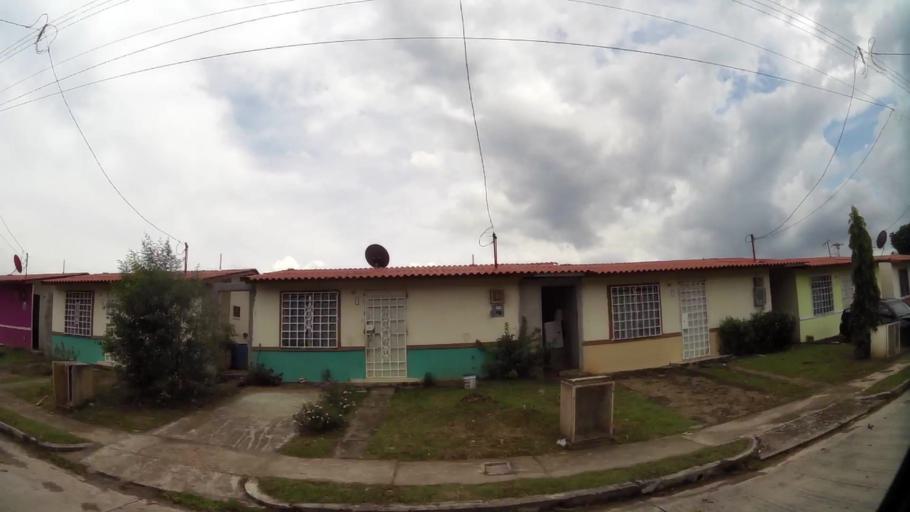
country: PA
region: Panama
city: Cabra Numero Uno
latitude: 9.1165
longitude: -79.3250
